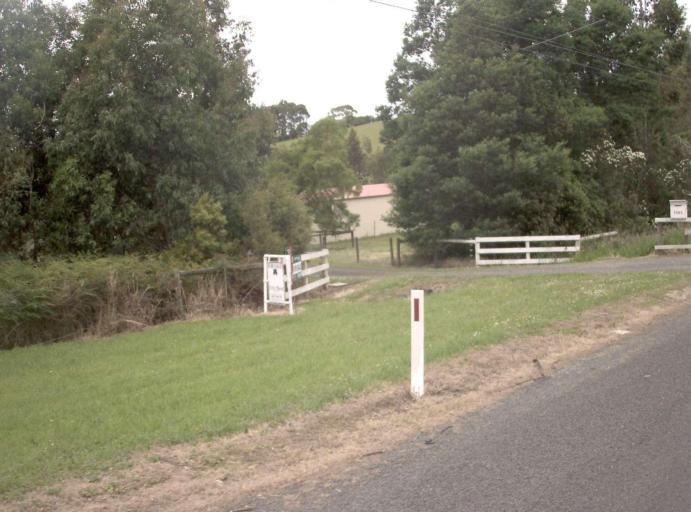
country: AU
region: Victoria
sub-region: Baw Baw
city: Warragul
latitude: -38.4485
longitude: 145.8817
